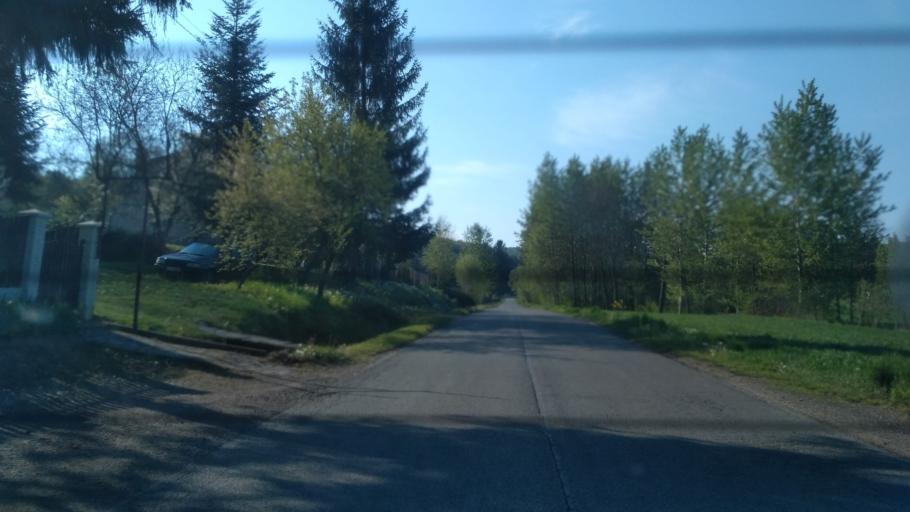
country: PL
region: Subcarpathian Voivodeship
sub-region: Powiat jaroslawski
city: Pruchnik
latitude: 49.8732
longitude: 22.5655
